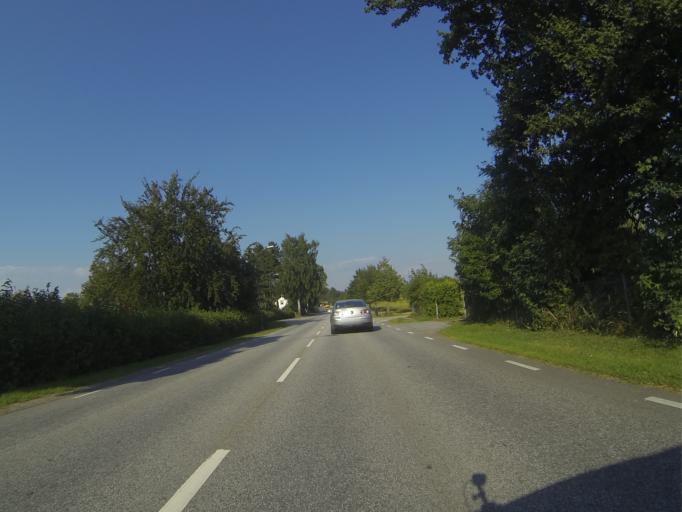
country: SE
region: Skane
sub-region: Svedala Kommun
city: Klagerup
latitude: 55.5774
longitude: 13.1895
